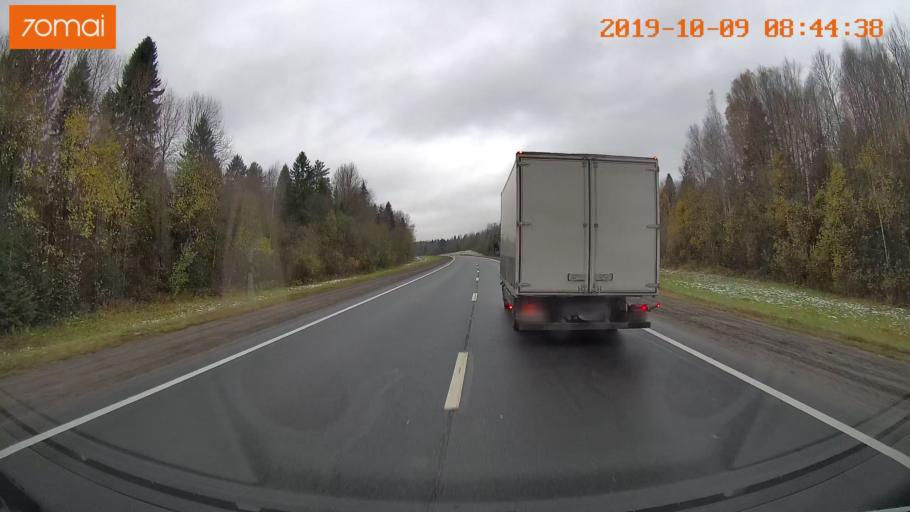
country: RU
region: Vologda
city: Gryazovets
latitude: 59.0390
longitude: 40.1059
